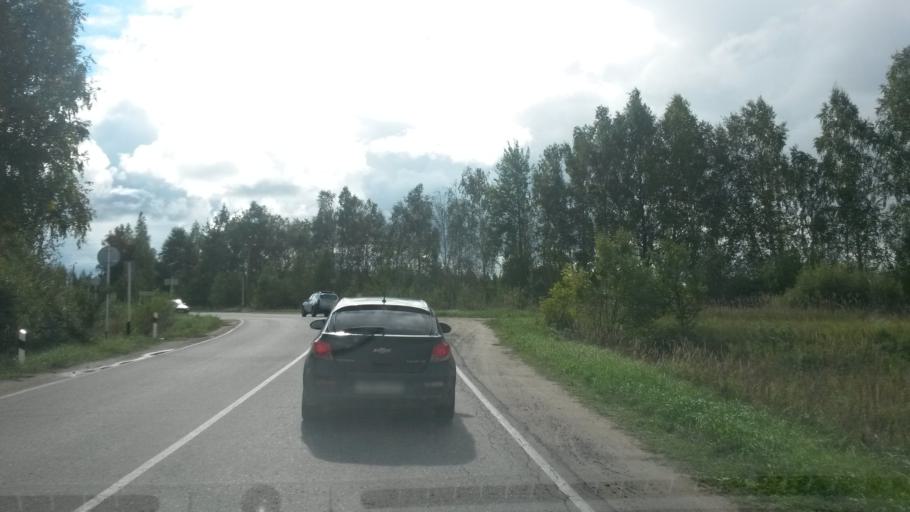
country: RU
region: Ivanovo
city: Zavolzhsk
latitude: 57.5021
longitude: 42.1140
